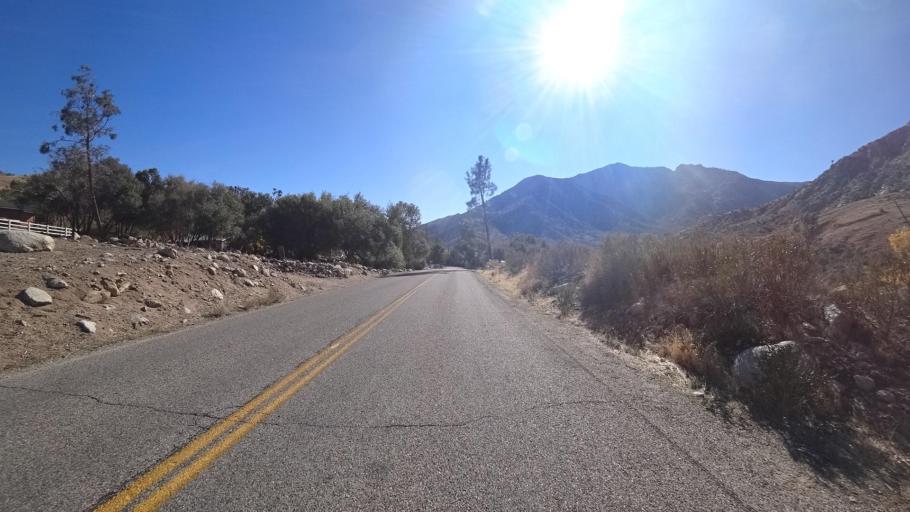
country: US
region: California
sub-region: Kern County
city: Kernville
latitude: 35.7911
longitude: -118.4479
